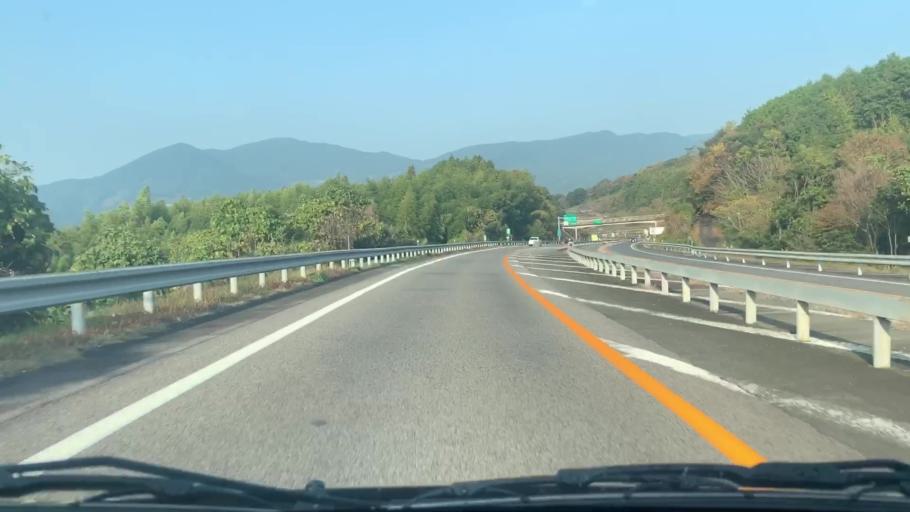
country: JP
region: Saga Prefecture
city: Imaricho-ko
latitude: 33.1665
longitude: 129.8576
